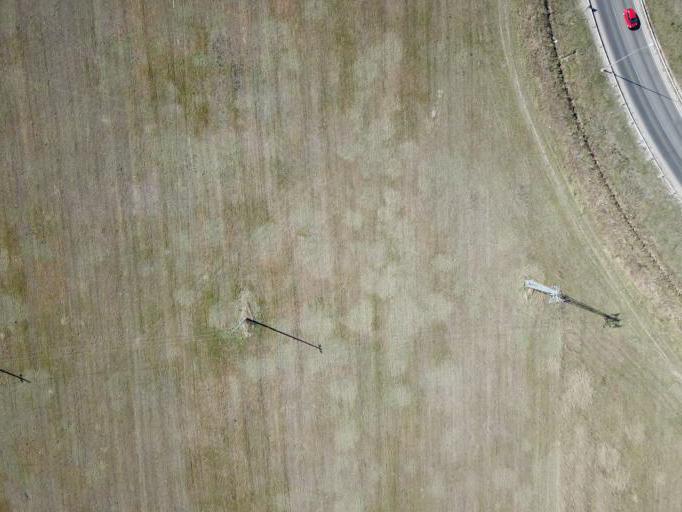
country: HU
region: Pest
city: Budakalasz
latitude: 47.6110
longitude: 19.0684
